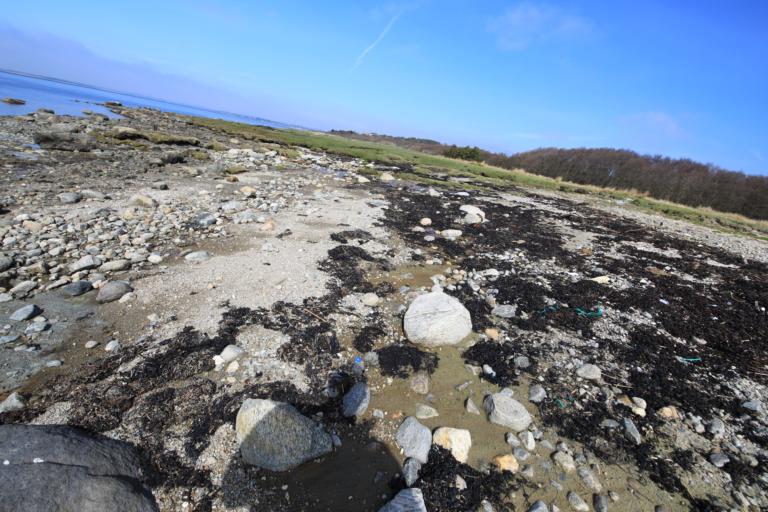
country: SE
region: Halland
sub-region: Kungsbacka Kommun
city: Frillesas
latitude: 57.2853
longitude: 12.1640
